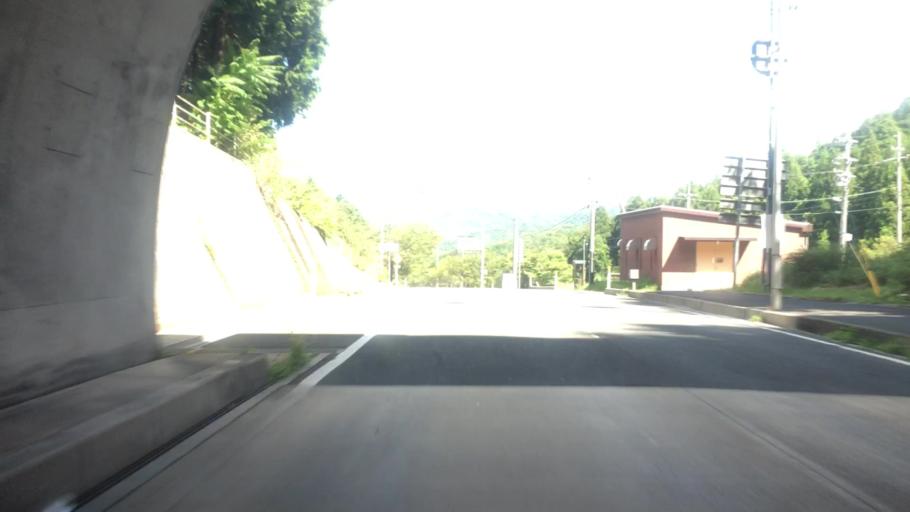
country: JP
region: Kyoto
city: Miyazu
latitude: 35.5776
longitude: 135.0081
